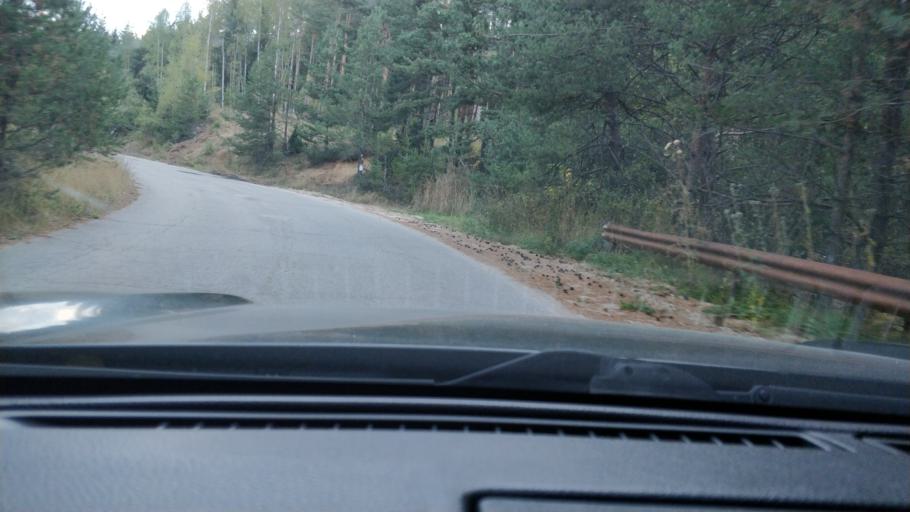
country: BG
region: Sofiya
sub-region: Obshtina Samokov
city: Samokov
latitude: 42.4836
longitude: 23.3887
